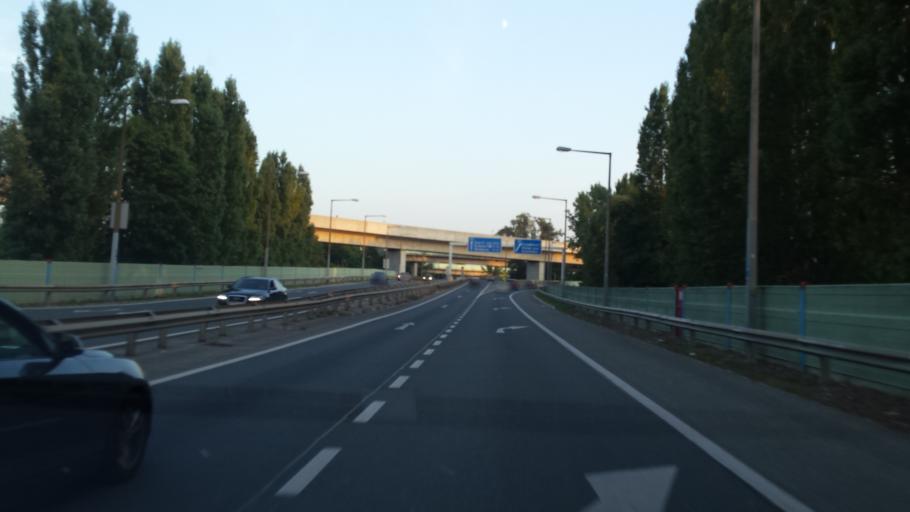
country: AT
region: Vienna
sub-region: Wien Stadt
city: Vienna
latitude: 48.2174
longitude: 16.4447
